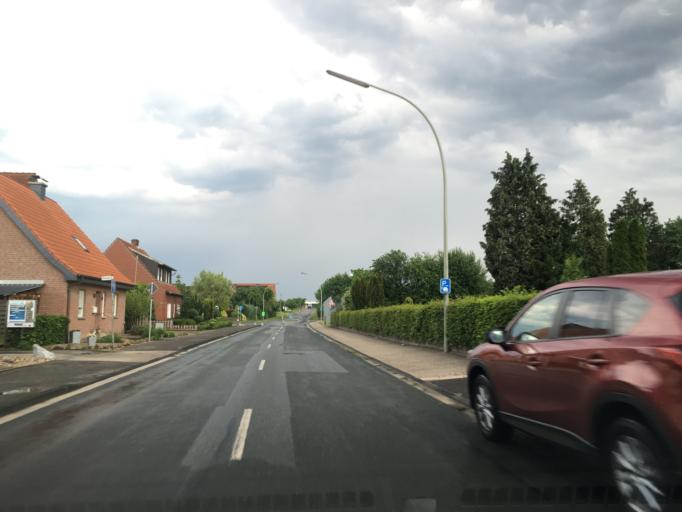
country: DE
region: North Rhine-Westphalia
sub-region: Regierungsbezirk Munster
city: Nordwalde
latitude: 52.0805
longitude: 7.4779
